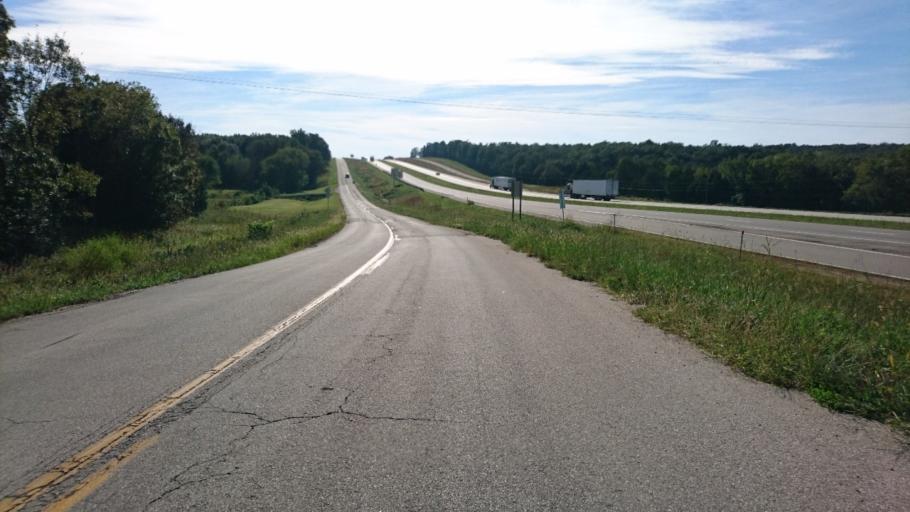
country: US
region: Missouri
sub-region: Crawford County
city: Bourbon
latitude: 38.1178
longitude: -91.3183
